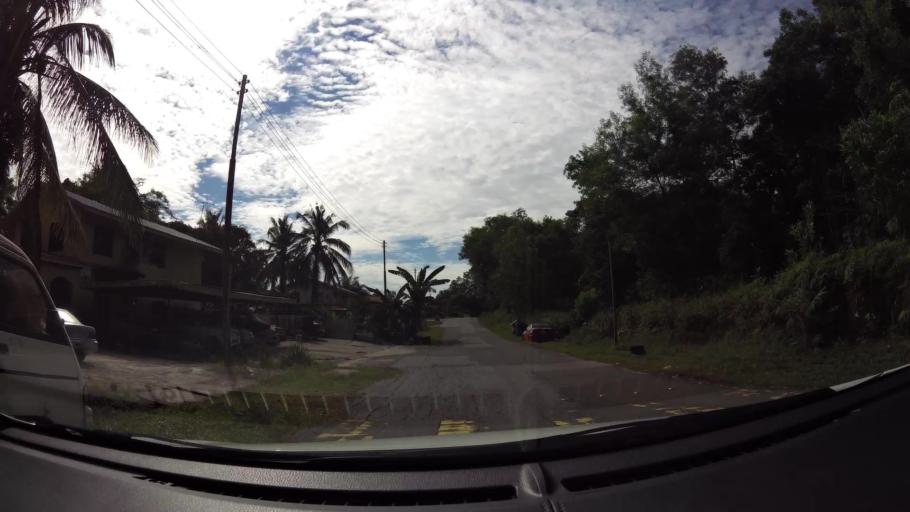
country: BN
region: Brunei and Muara
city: Bandar Seri Begawan
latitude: 4.9217
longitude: 114.8999
